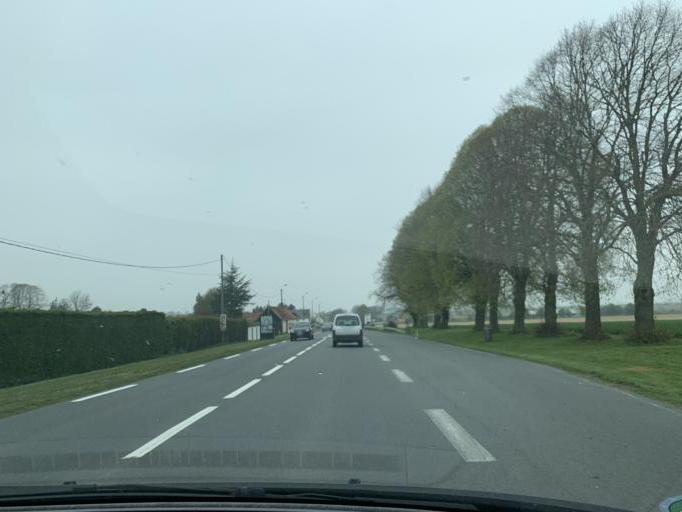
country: FR
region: Picardie
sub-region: Departement de la Somme
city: Abbeville
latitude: 50.1511
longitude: 1.8202
